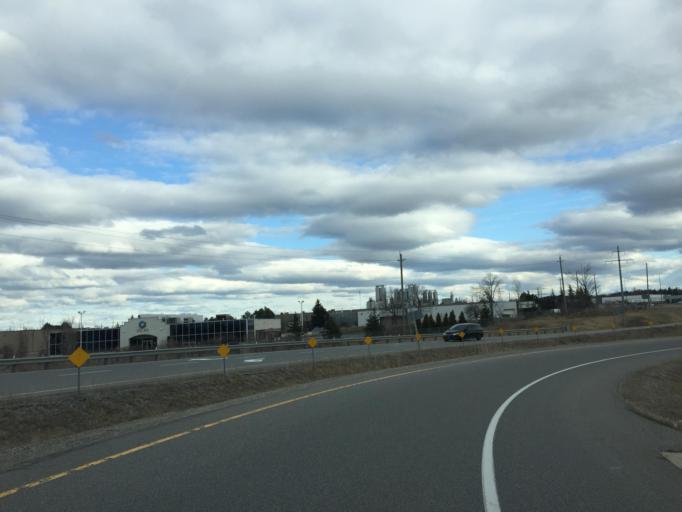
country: CA
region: Ontario
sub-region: Wellington County
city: Guelph
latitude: 43.4909
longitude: -80.2112
